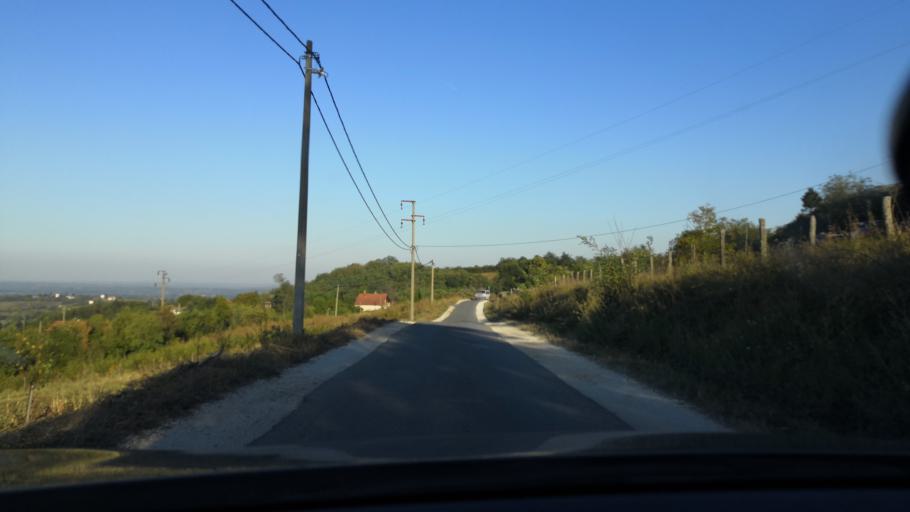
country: RS
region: Central Serbia
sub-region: Sumadijski Okrug
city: Arangelovac
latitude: 44.3321
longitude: 20.5719
